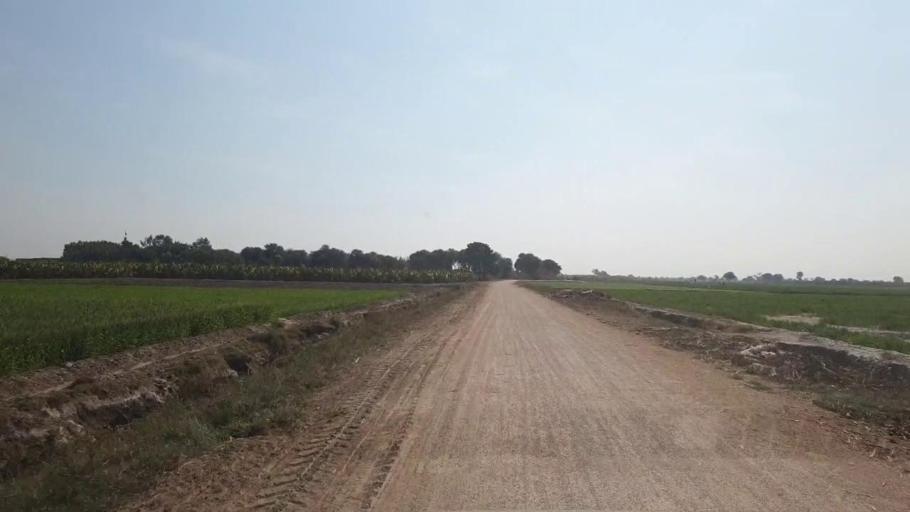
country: PK
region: Sindh
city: Chambar
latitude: 25.3486
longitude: 68.8358
